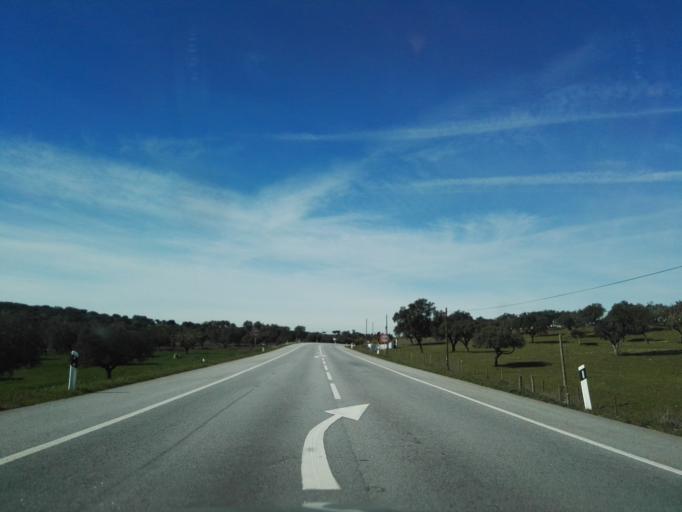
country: PT
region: Portalegre
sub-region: Portalegre
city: Urra
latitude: 39.1900
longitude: -7.3556
